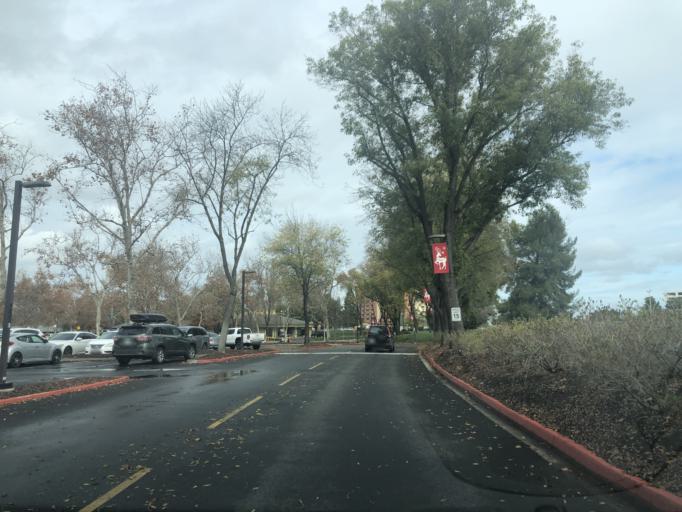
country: US
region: California
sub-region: Contra Costa County
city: Pleasant Hill
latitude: 37.9684
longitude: -122.0553
